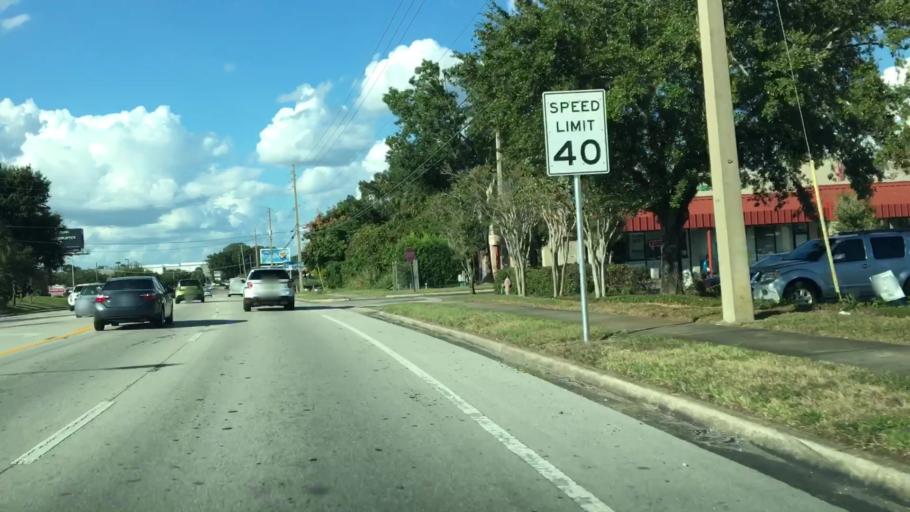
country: US
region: Florida
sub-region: Orange County
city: Edgewood
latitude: 28.4958
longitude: -81.3750
